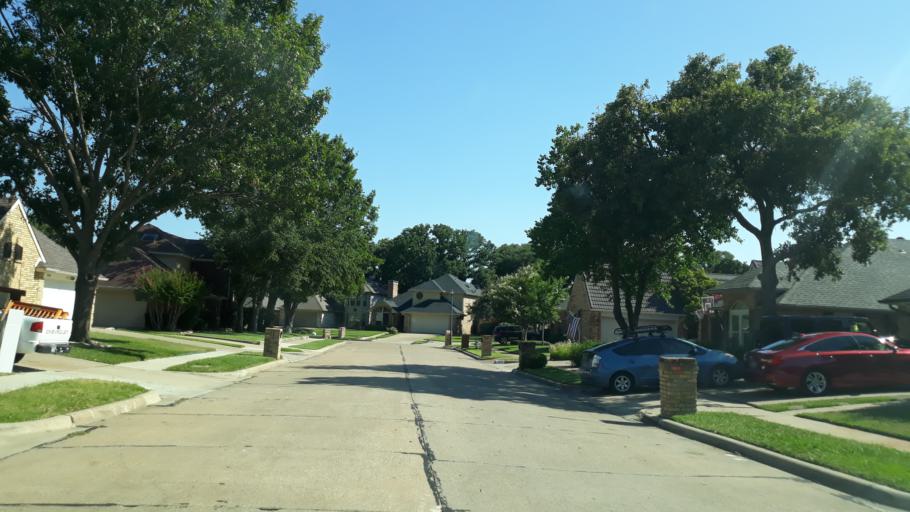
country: US
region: Texas
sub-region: Dallas County
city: Irving
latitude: 32.8311
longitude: -97.0059
